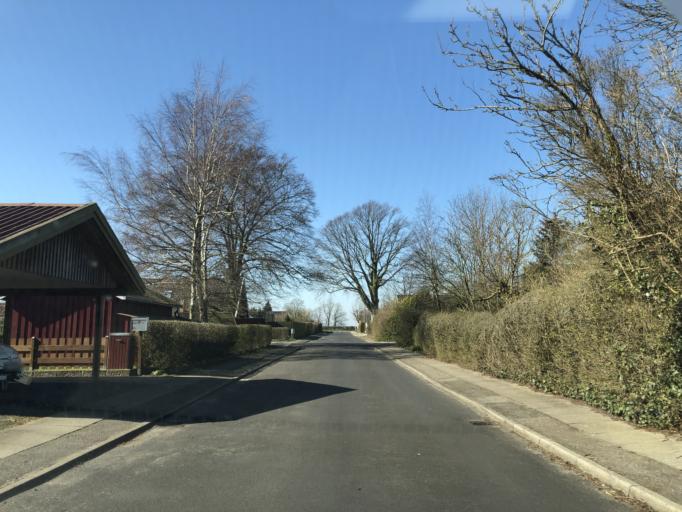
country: DK
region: Capital Region
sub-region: Dragor Kommune
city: Dragor
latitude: 55.5863
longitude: 12.6384
